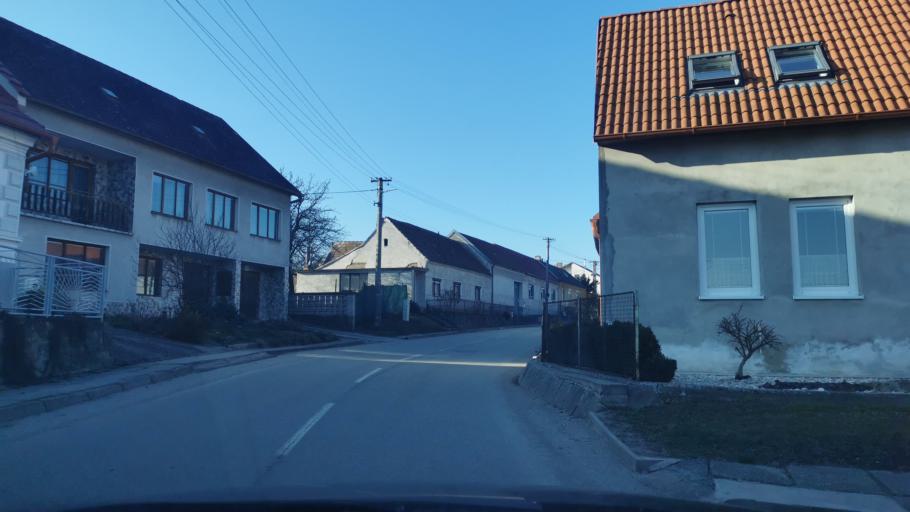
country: SK
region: Trnavsky
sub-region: Okres Senica
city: Senica
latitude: 48.7454
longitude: 17.3543
